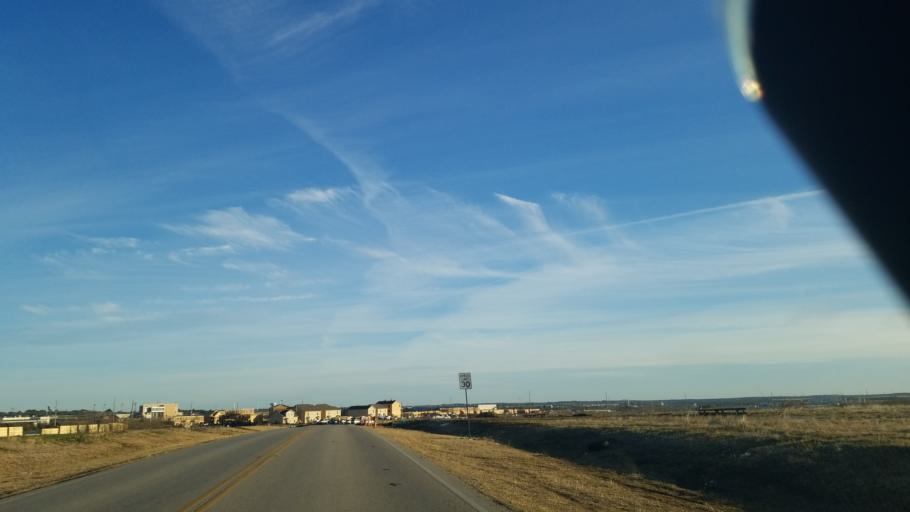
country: US
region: Texas
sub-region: Denton County
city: Denton
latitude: 33.2170
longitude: -97.1753
